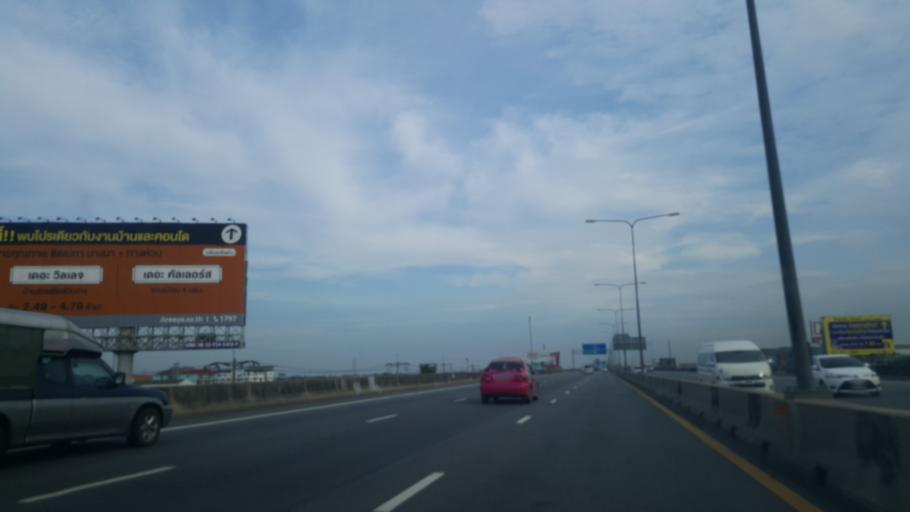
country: TH
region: Bangkok
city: Bang Na
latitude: 13.6548
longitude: 100.6734
